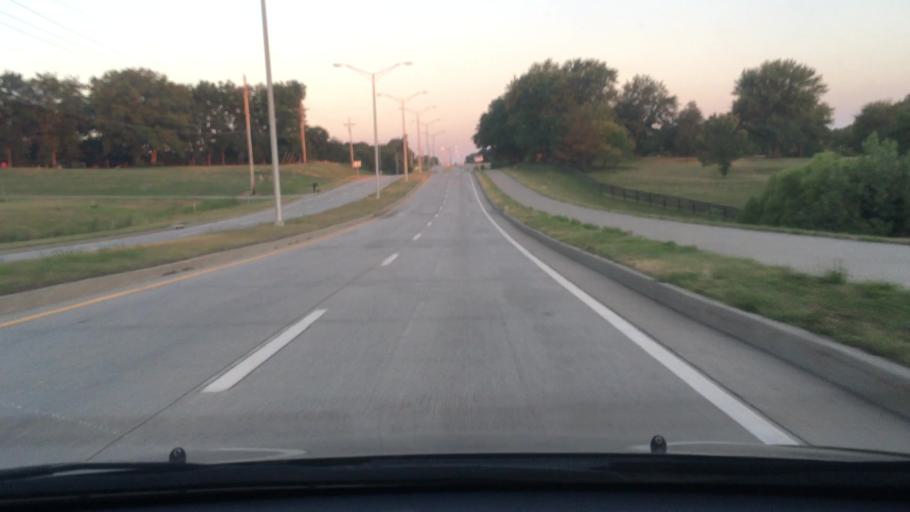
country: US
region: Missouri
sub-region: Cass County
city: Raymore
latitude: 38.8540
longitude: -94.4243
